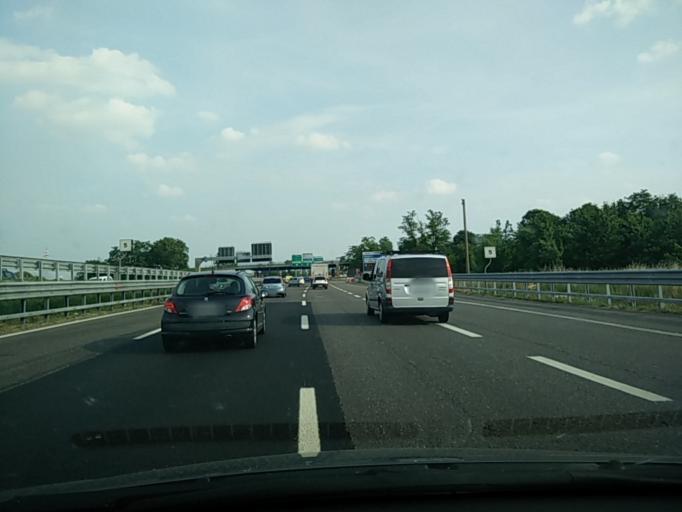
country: IT
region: Lombardy
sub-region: Citta metropolitana di Milano
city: Figino
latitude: 45.5045
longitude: 9.0651
